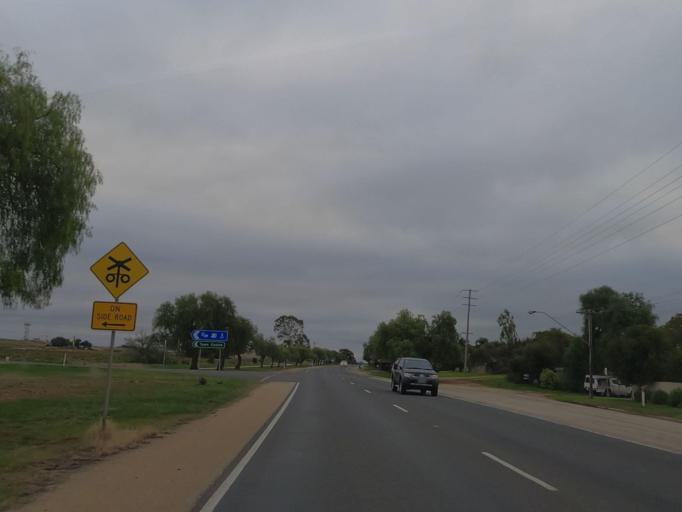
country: AU
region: Victoria
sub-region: Swan Hill
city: Swan Hill
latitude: -35.4580
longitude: 143.6309
